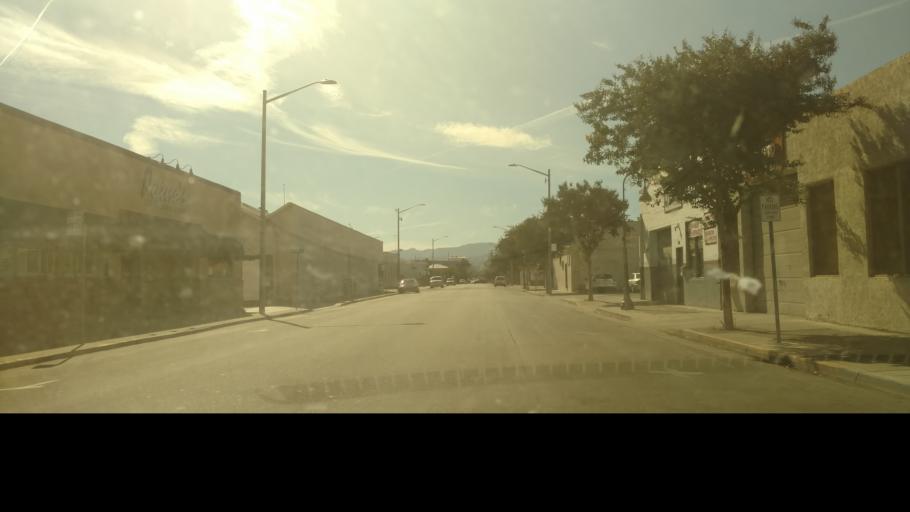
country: US
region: California
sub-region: San Benito County
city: Hollister
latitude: 36.8524
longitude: -121.4010
